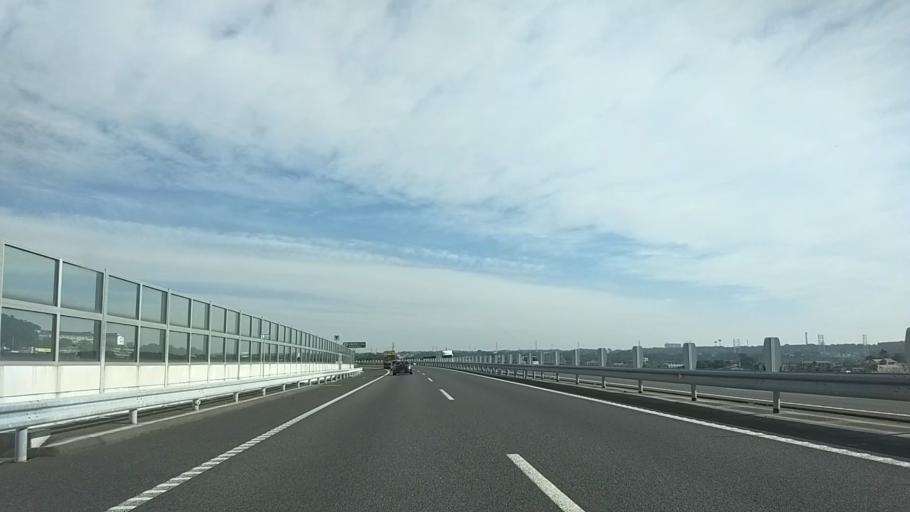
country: JP
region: Kanagawa
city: Zama
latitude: 35.5036
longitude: 139.3656
